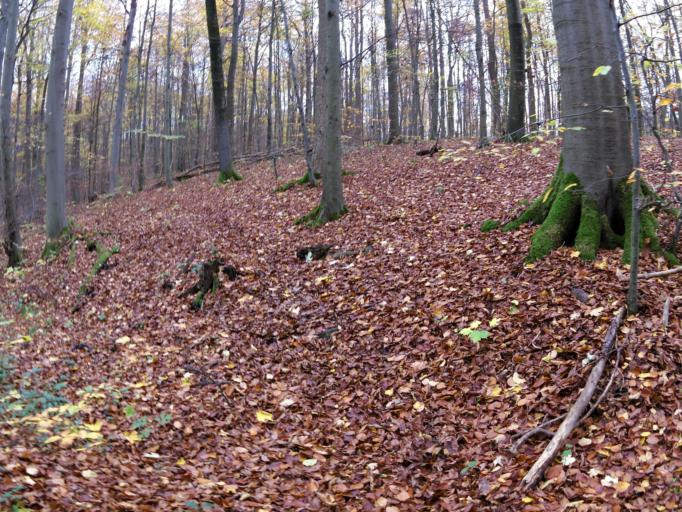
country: DE
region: Thuringia
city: Bischofroda
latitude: 51.0782
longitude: 10.3816
